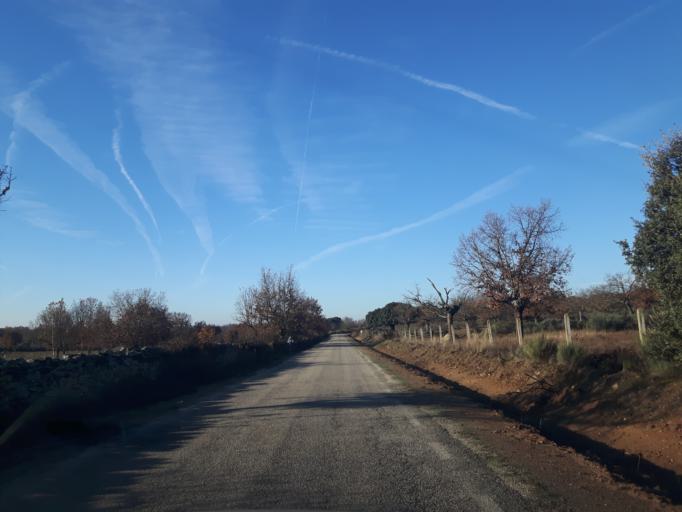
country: ES
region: Castille and Leon
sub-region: Provincia de Salamanca
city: Cerralbo
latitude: 40.9453
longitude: -6.6107
